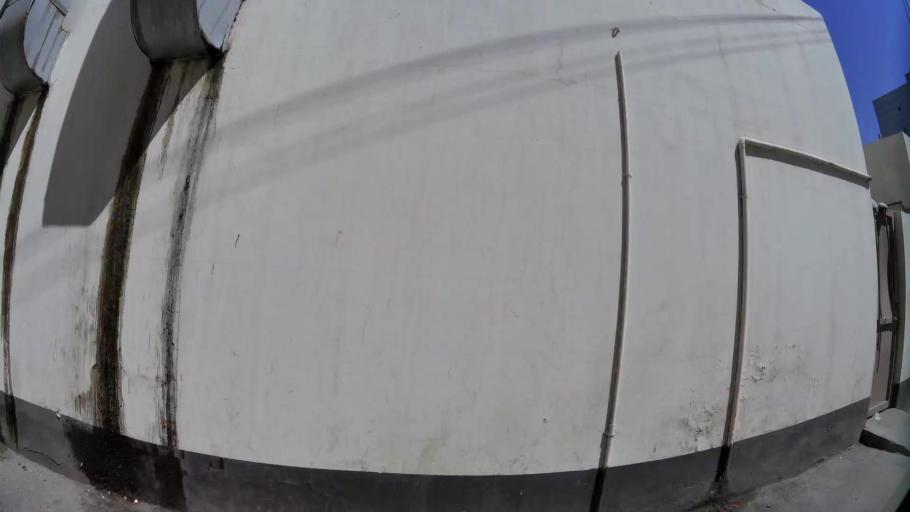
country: BH
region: Manama
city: Manama
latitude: 26.2050
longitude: 50.5991
